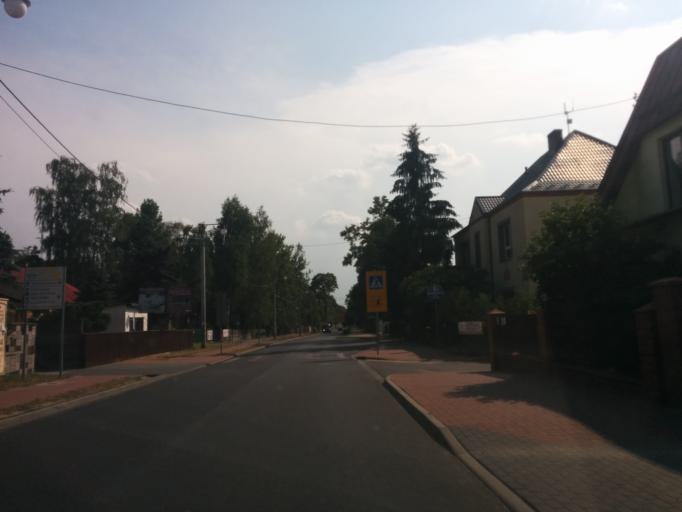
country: PL
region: Silesian Voivodeship
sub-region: Powiat czestochowski
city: Olsztyn
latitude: 50.7481
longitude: 19.2680
